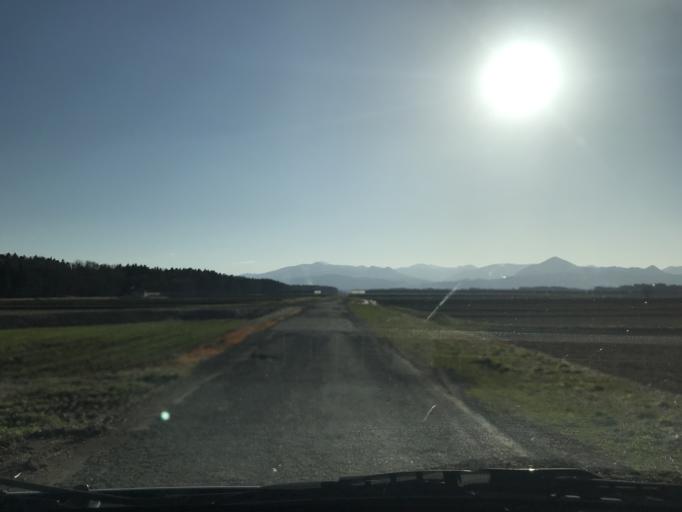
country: JP
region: Iwate
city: Kitakami
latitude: 39.2698
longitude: 141.0607
